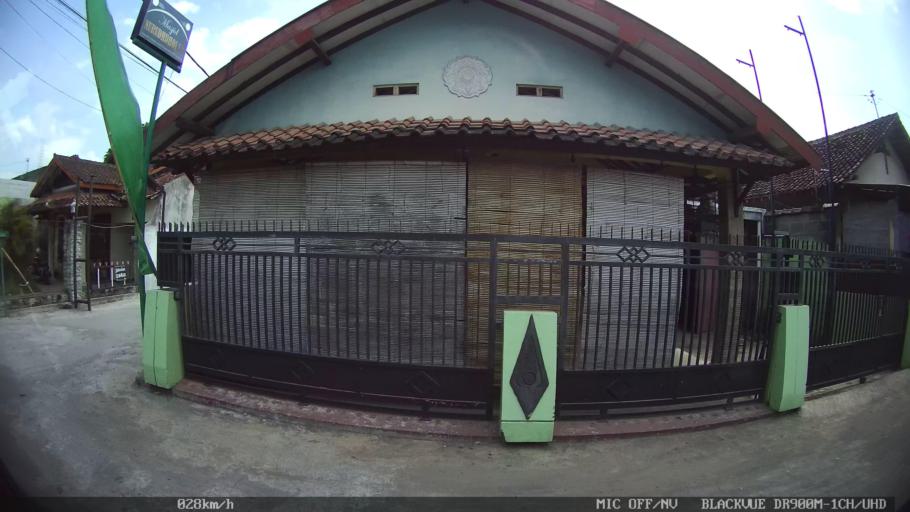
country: ID
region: Daerah Istimewa Yogyakarta
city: Kasihan
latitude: -7.8198
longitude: 110.3324
